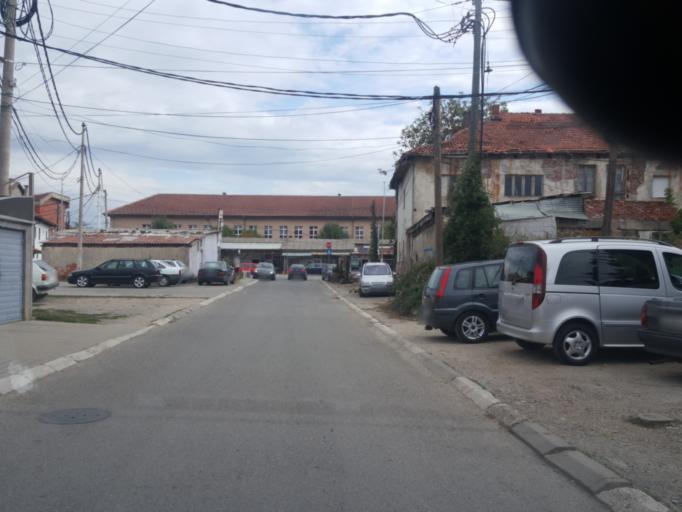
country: XK
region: Gjakova
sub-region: Komuna e Gjakoves
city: Gjakove
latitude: 42.3891
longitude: 20.4258
